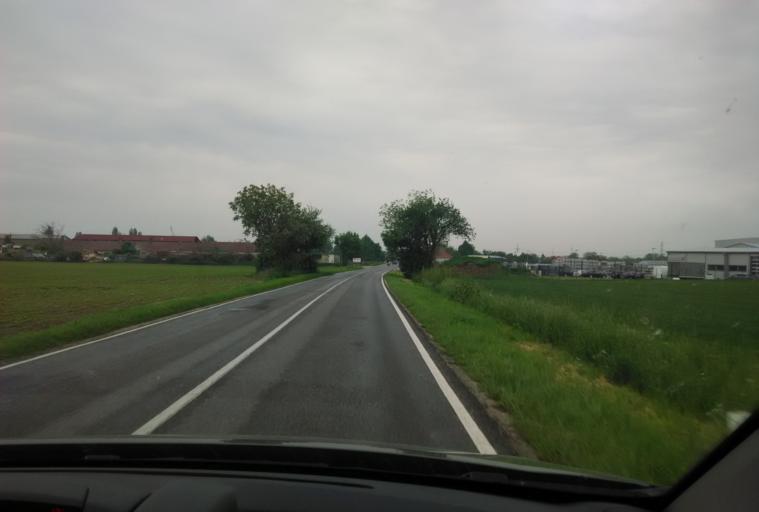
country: SK
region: Trnavsky
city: Leopoldov
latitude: 48.4552
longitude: 17.6864
